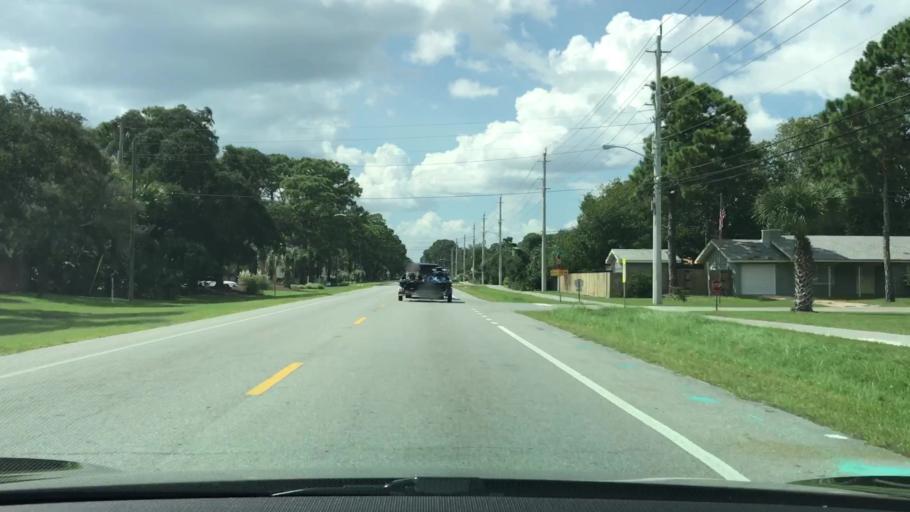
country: US
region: Florida
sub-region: Bay County
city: Lower Grand Lagoon
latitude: 30.1597
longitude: -85.7623
